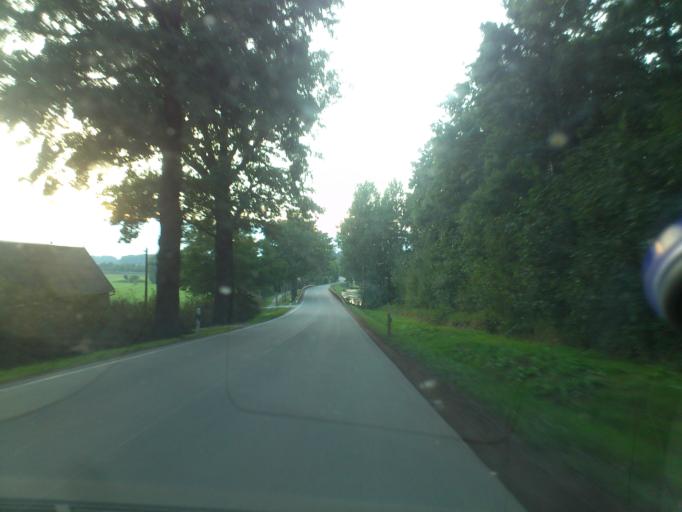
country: DE
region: Saxony
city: Jahnsdorf
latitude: 50.7604
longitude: 12.8458
